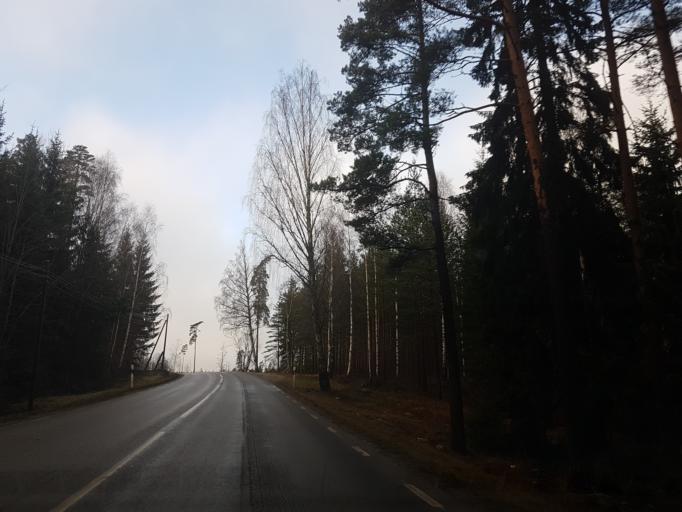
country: SE
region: Stockholm
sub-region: Nykvarns Kommun
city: Nykvarn
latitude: 59.2065
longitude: 17.3867
